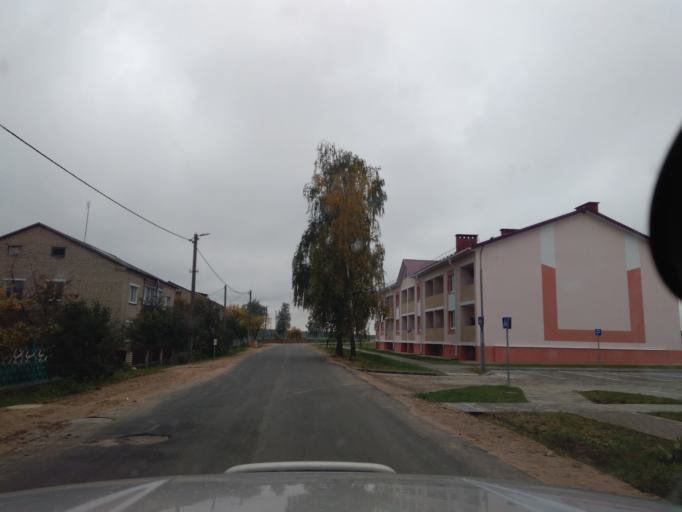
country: BY
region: Minsk
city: Kapyl'
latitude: 53.1395
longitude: 27.0901
